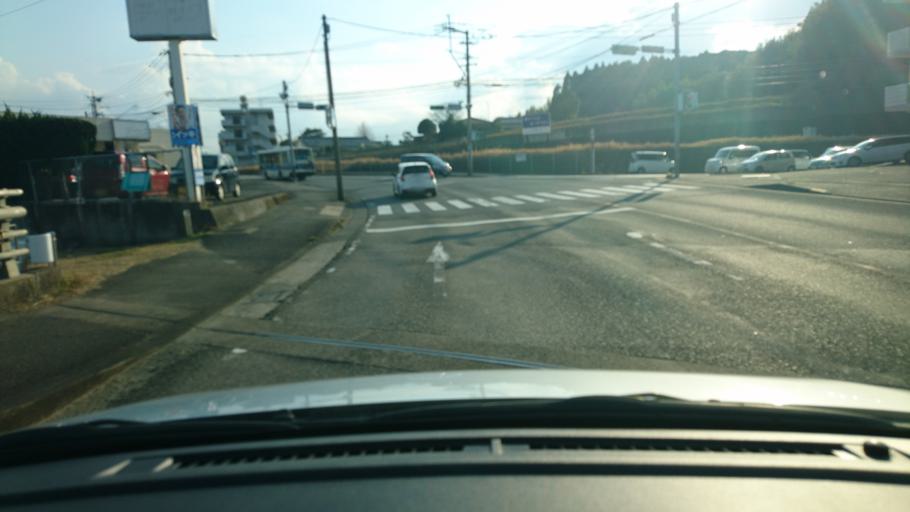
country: JP
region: Miyazaki
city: Miyazaki-shi
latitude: 31.8837
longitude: 131.4084
